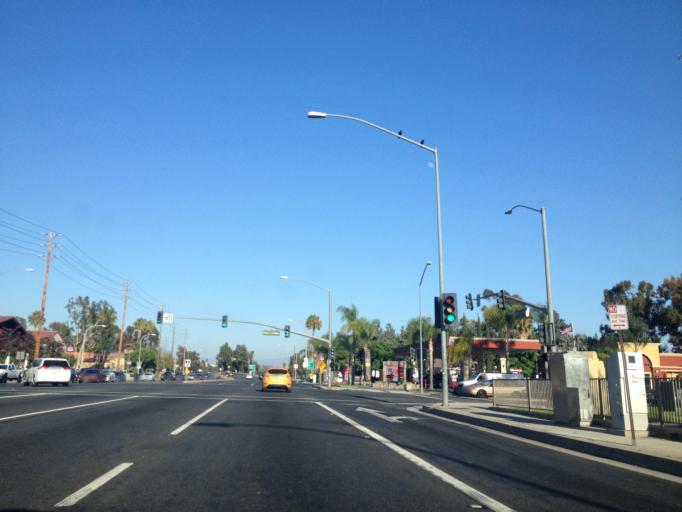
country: US
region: California
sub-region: Orange County
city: Brea
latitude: 33.9120
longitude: -117.8885
